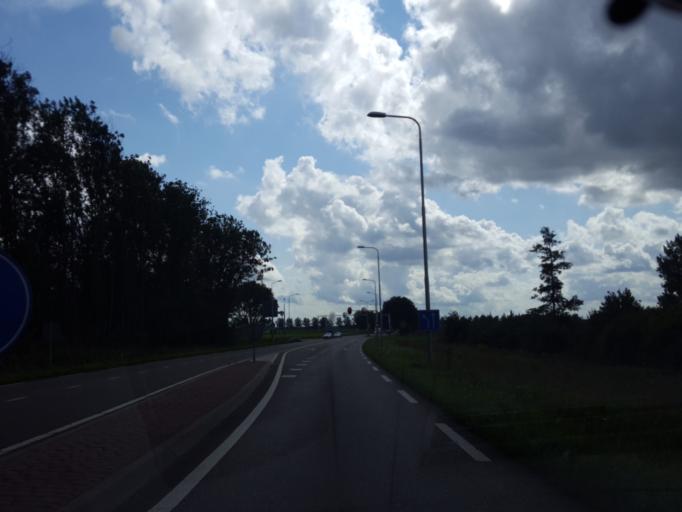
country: NL
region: Gelderland
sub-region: Gemeente Beuningen
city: Beuningen
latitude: 51.8483
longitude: 5.7456
